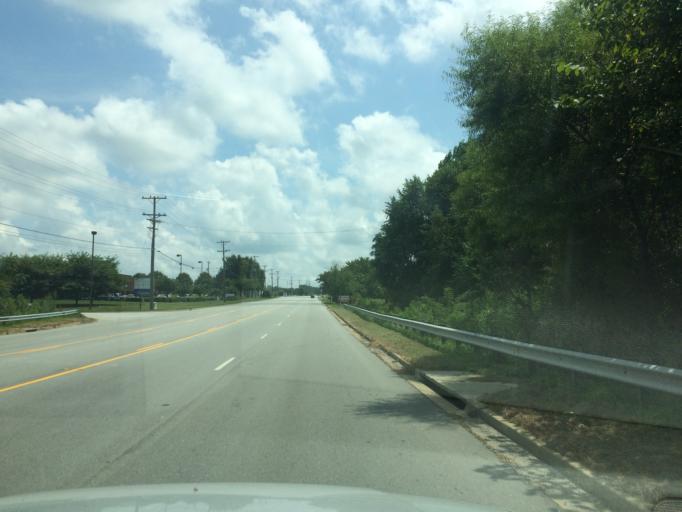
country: US
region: South Carolina
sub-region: Spartanburg County
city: Duncan
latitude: 34.8736
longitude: -82.1446
